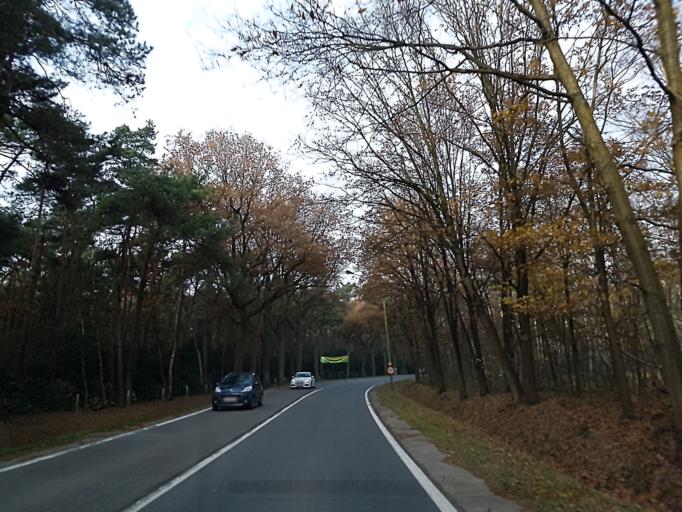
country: BE
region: Flanders
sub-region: Provincie Antwerpen
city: Kalmthout
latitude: 51.4098
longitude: 4.4640
